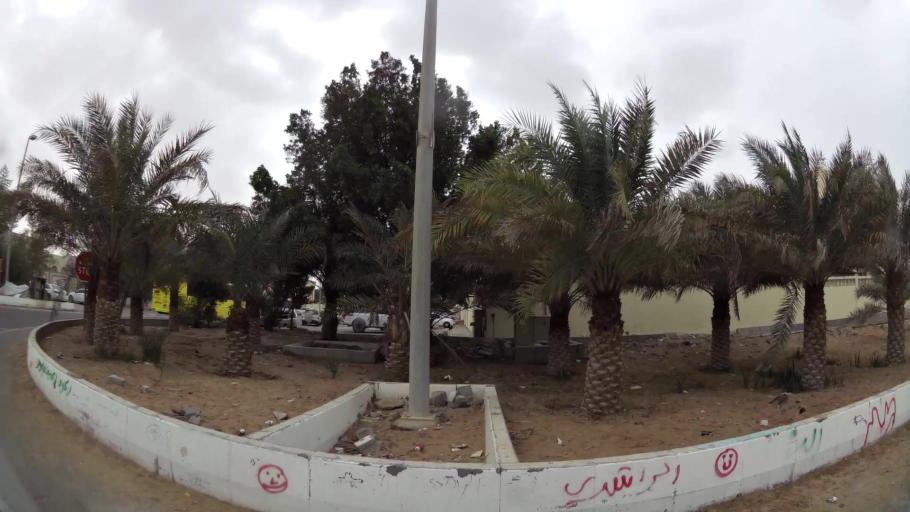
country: AE
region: Abu Dhabi
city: Abu Dhabi
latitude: 24.3565
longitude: 54.6533
